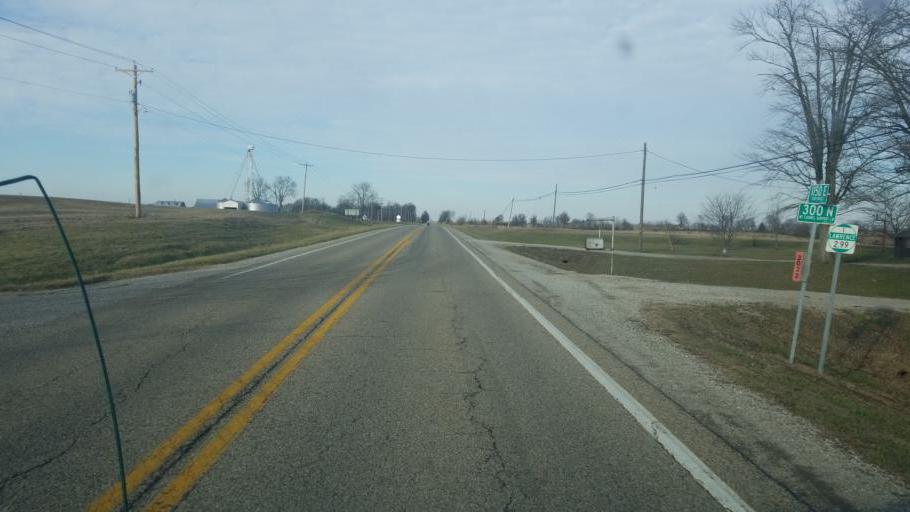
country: US
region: Illinois
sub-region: Lawrence County
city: Bridgeport
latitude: 38.6119
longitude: -87.6943
